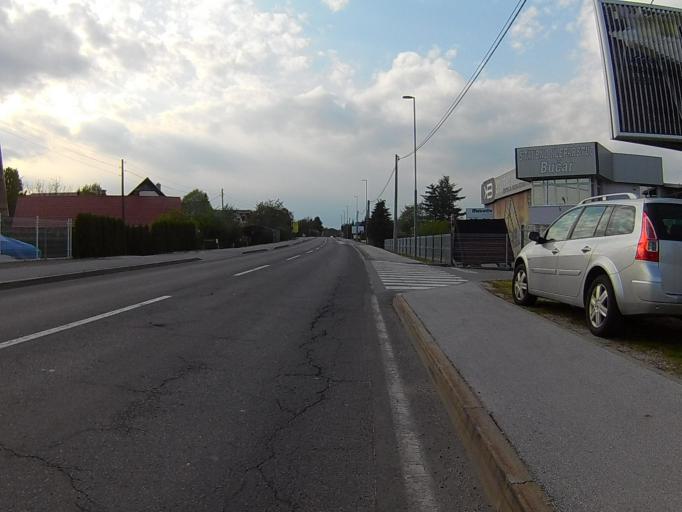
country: SI
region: Miklavz na Dravskem Polju
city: Miklavz na Dravskem Polju
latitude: 46.5066
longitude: 15.6975
